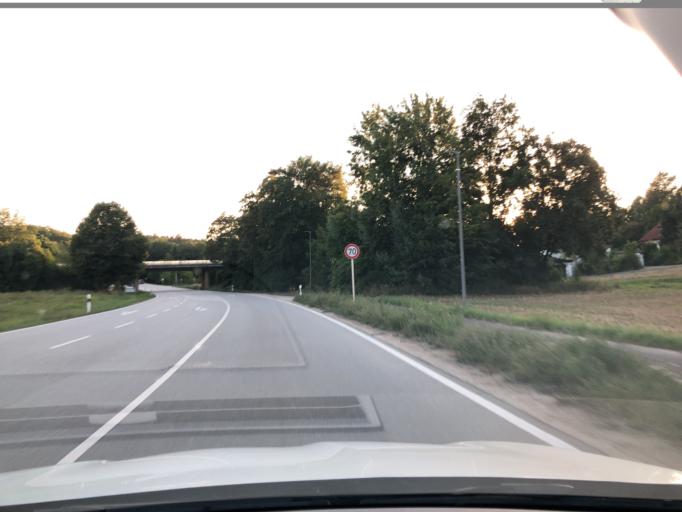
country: DE
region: Bavaria
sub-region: Upper Palatinate
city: Sulzbach-Rosenberg
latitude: 49.4983
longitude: 11.7324
